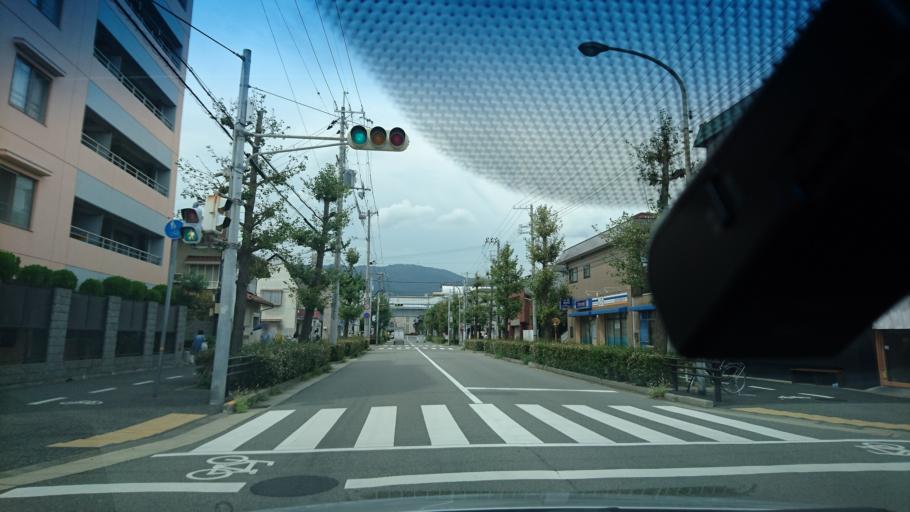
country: JP
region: Hyogo
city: Ashiya
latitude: 34.7291
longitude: 135.3179
